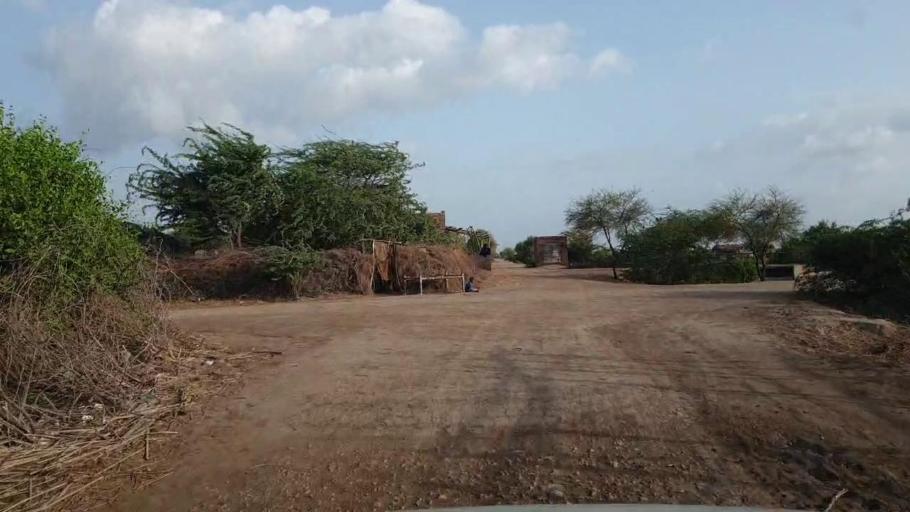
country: PK
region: Sindh
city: Kario
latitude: 24.8077
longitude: 68.6471
